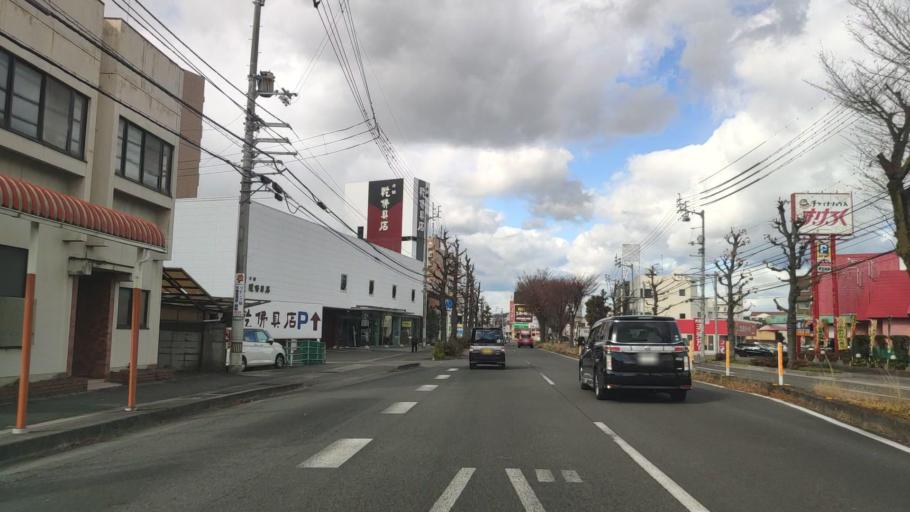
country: JP
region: Ehime
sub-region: Shikoku-chuo Shi
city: Matsuyama
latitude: 33.8144
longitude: 132.7777
